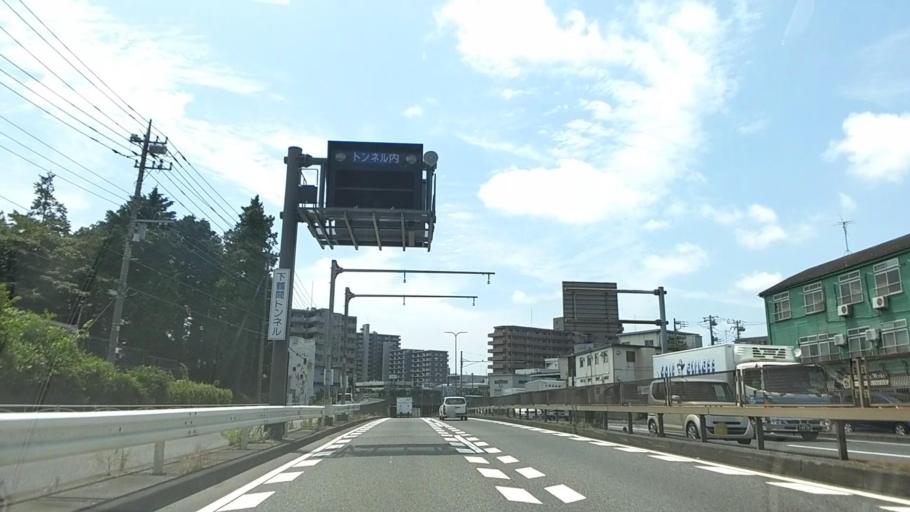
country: JP
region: Kanagawa
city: Minami-rinkan
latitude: 35.4931
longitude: 139.4643
